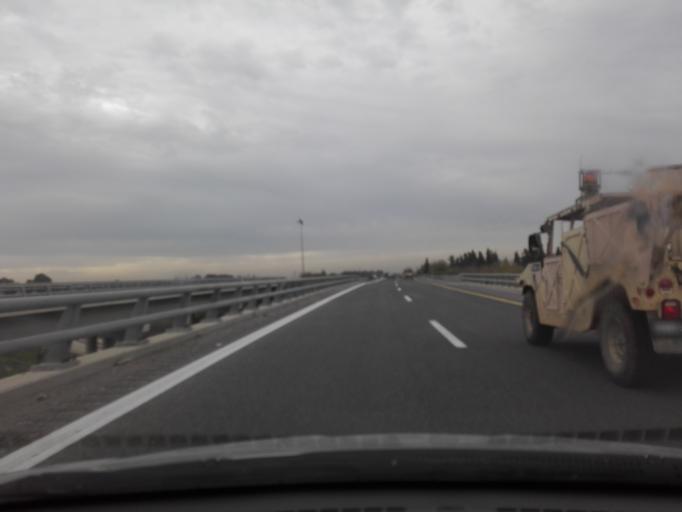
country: IL
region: Central District
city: Mazkeret Batya
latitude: 31.8518
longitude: 34.8700
